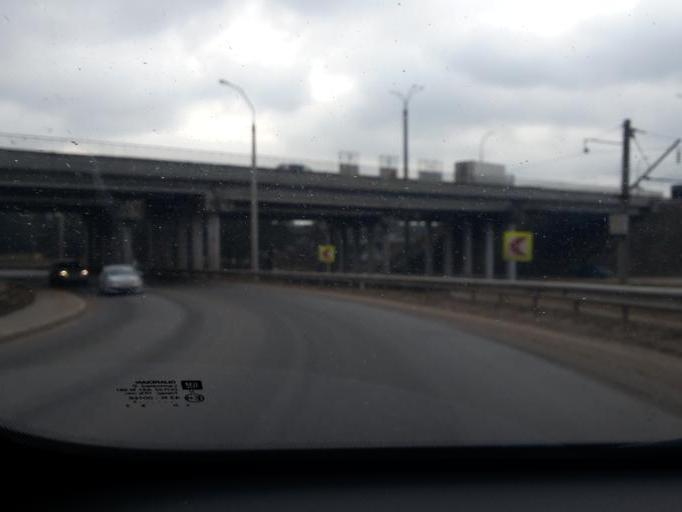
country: BY
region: Minsk
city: Vyaliki Trastsyanets
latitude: 53.9221
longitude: 27.6800
